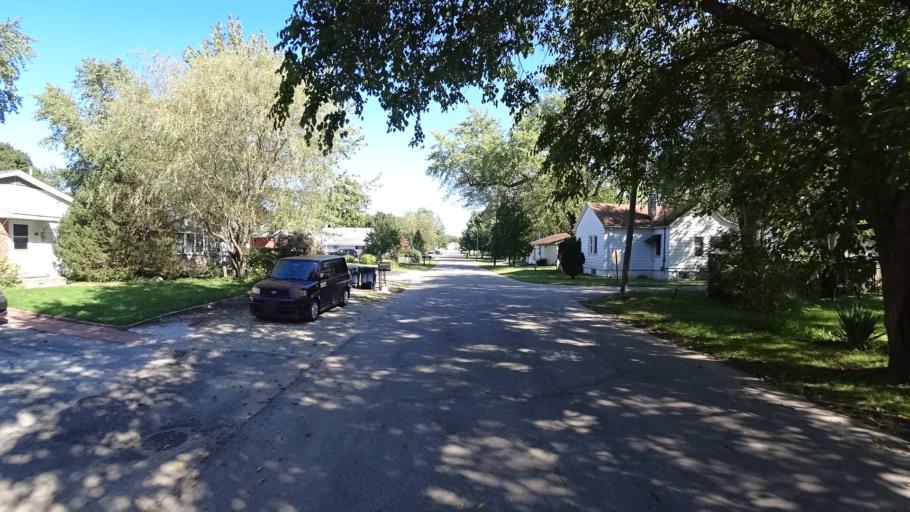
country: US
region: Indiana
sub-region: LaPorte County
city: Michigan City
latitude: 41.6930
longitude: -86.8974
